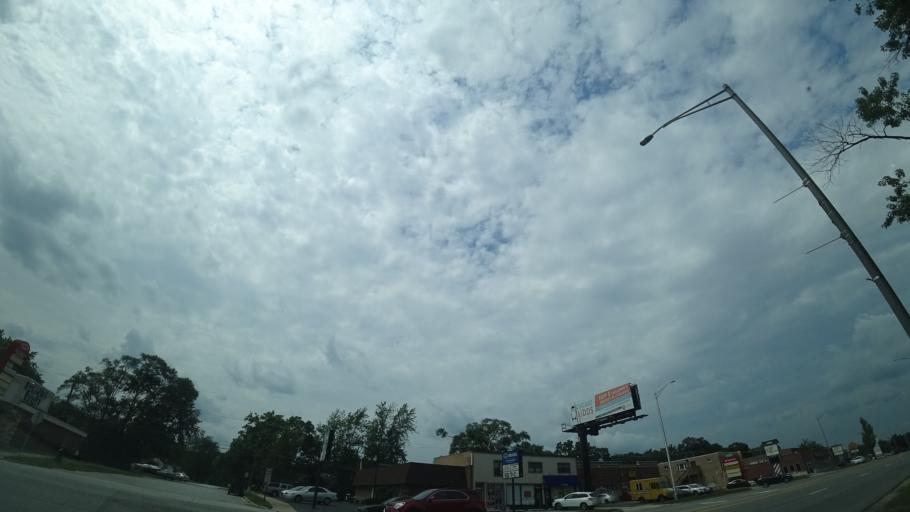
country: US
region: Illinois
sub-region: Cook County
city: Worth
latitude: 41.6862
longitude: -87.7972
